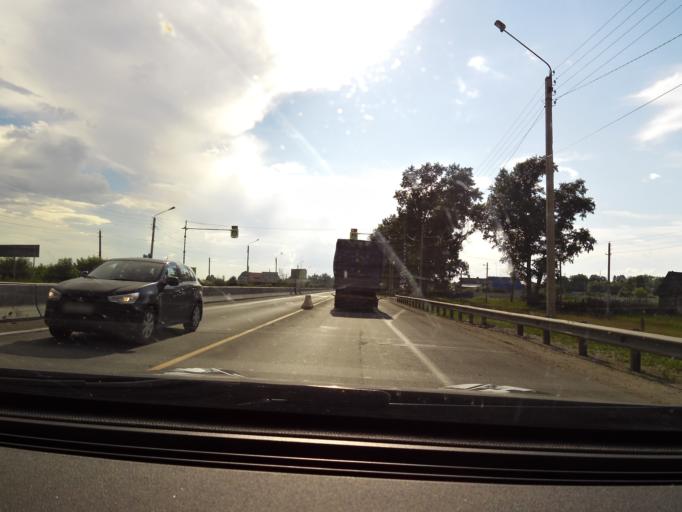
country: RU
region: Nizjnij Novgorod
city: Novosmolinskiy
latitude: 56.2773
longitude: 42.9954
